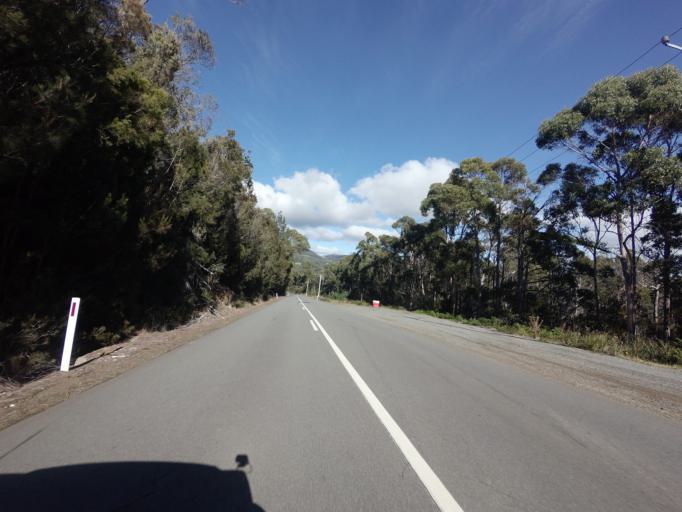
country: AU
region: Tasmania
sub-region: Clarence
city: Sandford
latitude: -43.0582
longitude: 147.8460
